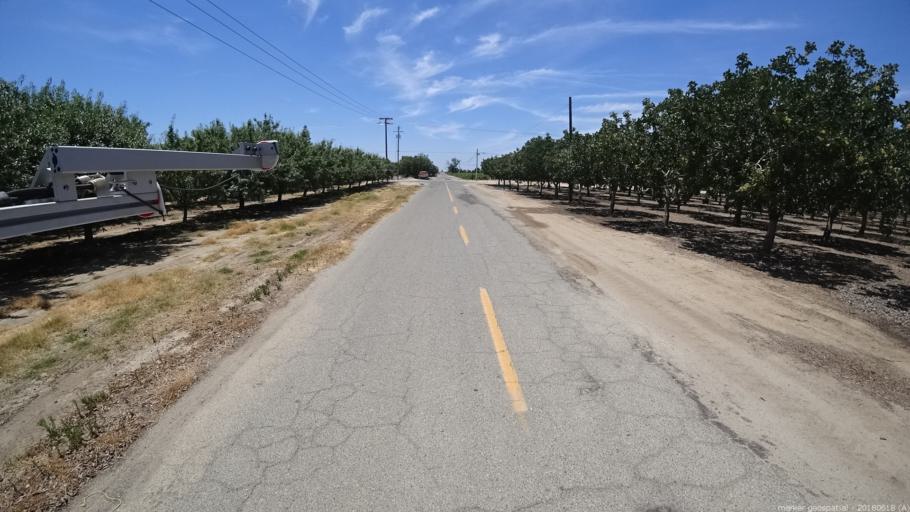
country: US
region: California
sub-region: Madera County
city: Madera
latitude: 36.9311
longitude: -120.0824
